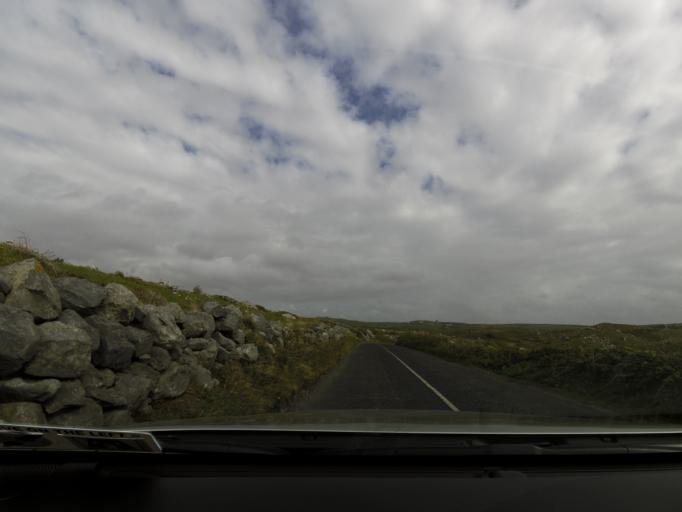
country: IE
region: Connaught
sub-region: County Galway
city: Bearna
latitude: 53.0592
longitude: -9.3598
